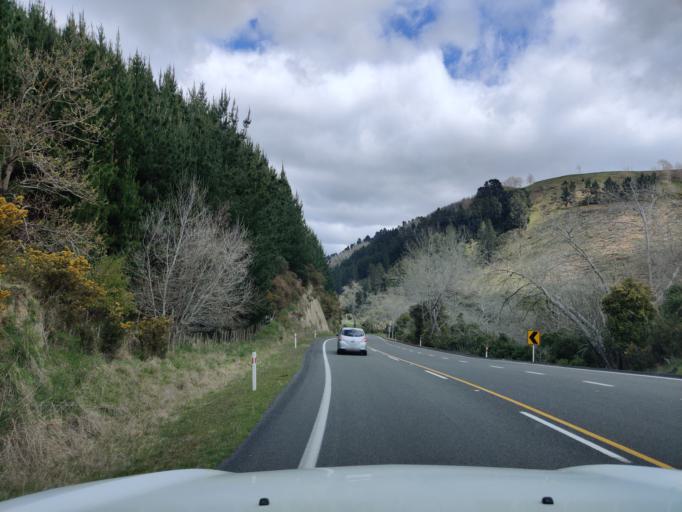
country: NZ
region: Manawatu-Wanganui
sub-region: Wanganui District
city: Wanganui
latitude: -39.8017
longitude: 175.1923
